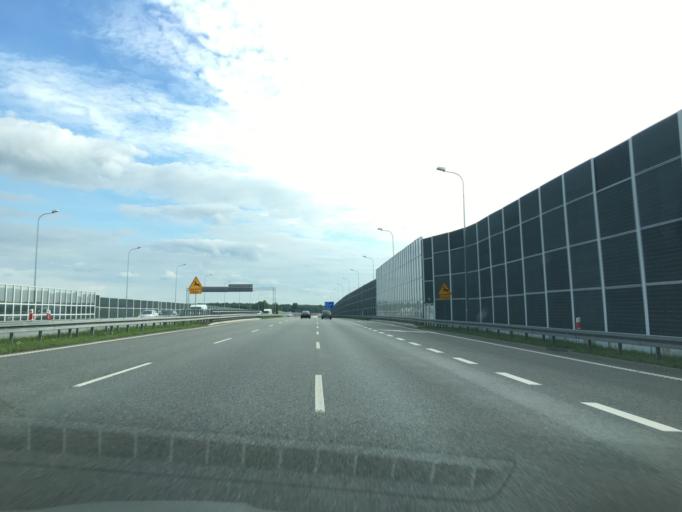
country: PL
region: Silesian Voivodeship
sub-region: Powiat tarnogorski
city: Wieszowa
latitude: 50.3443
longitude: 18.7255
